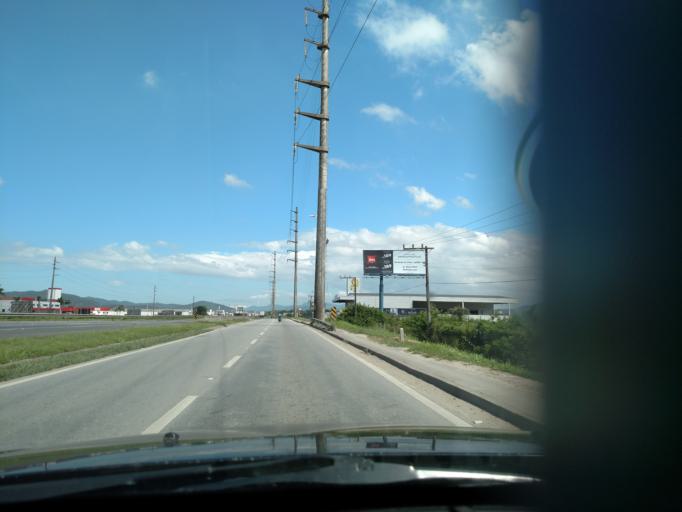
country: BR
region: Santa Catarina
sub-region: Itajai
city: Itajai
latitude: -26.9001
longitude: -48.7175
